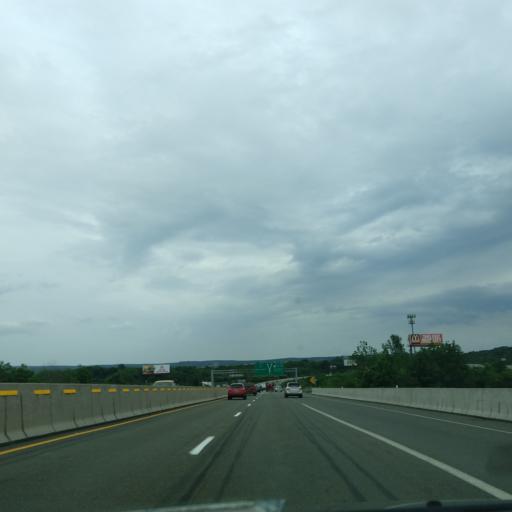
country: US
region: Pennsylvania
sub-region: Lackawanna County
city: Throop
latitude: 41.4495
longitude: -75.6371
